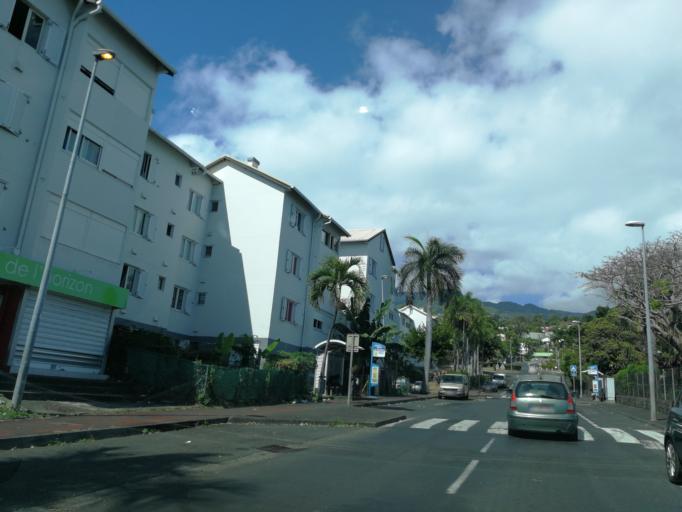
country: RE
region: Reunion
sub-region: Reunion
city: Saint-Denis
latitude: -20.9089
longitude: 55.4828
